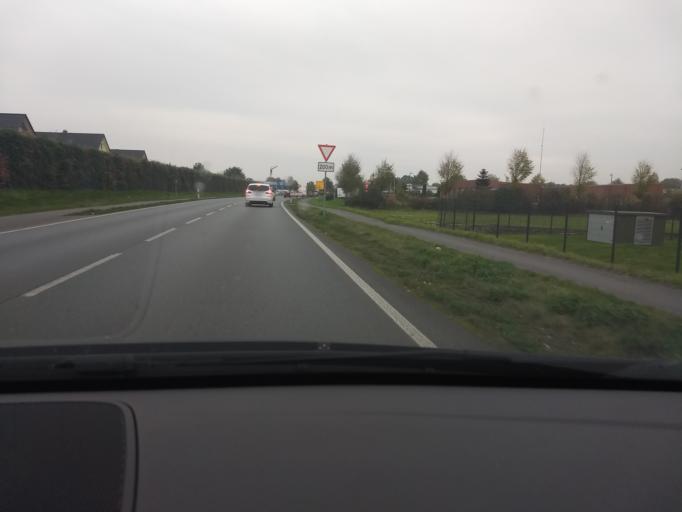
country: DE
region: North Rhine-Westphalia
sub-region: Regierungsbezirk Munster
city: Raesfeld
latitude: 51.7645
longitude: 6.8509
